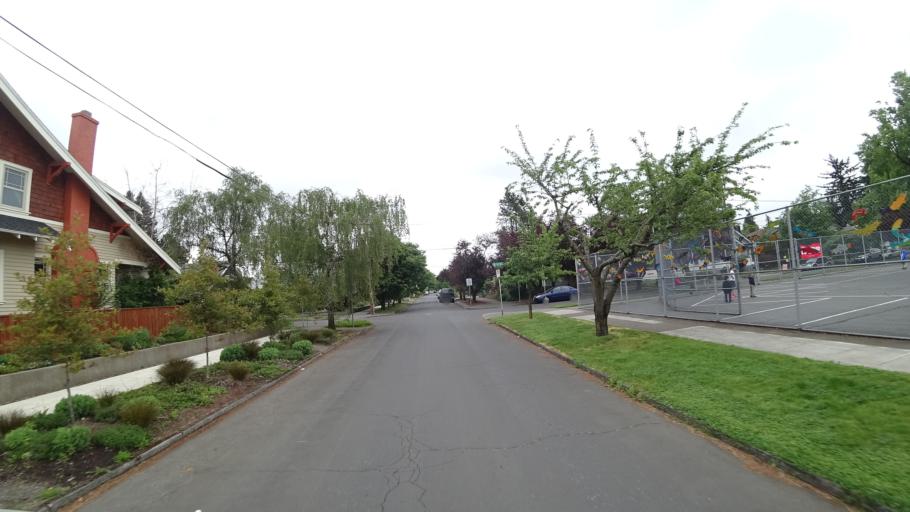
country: US
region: Oregon
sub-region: Multnomah County
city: Portland
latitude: 45.5437
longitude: -122.6080
